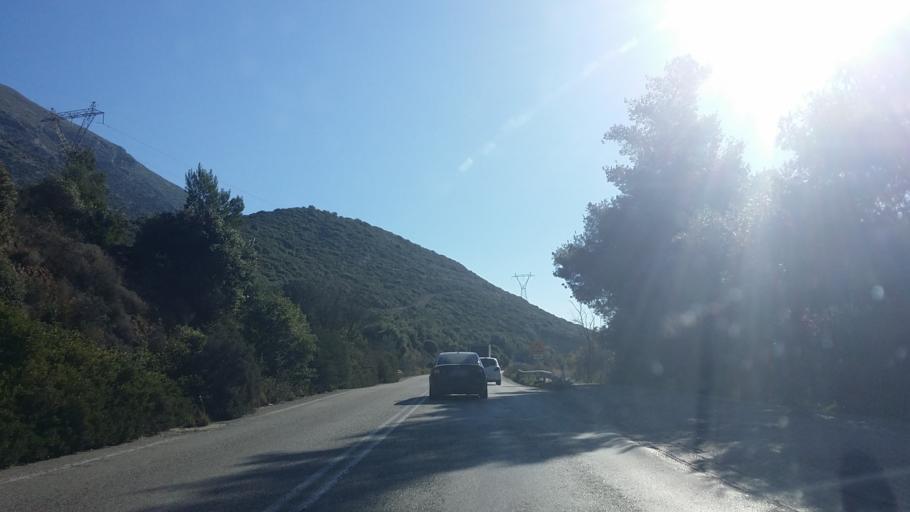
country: GR
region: West Greece
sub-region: Nomos Aitolias kai Akarnanias
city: Galatas
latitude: 38.3637
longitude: 21.6565
